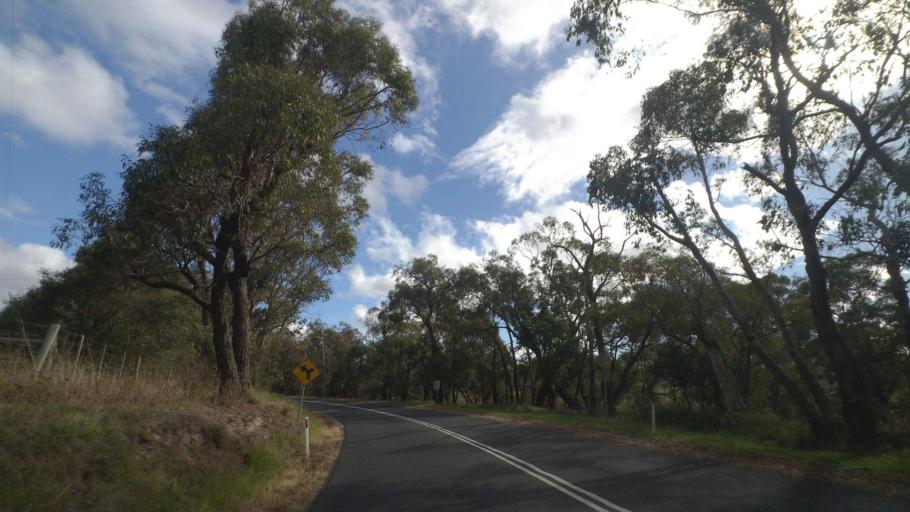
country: AU
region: Victoria
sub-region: Cardinia
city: Garfield
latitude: -38.0559
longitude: 145.6221
